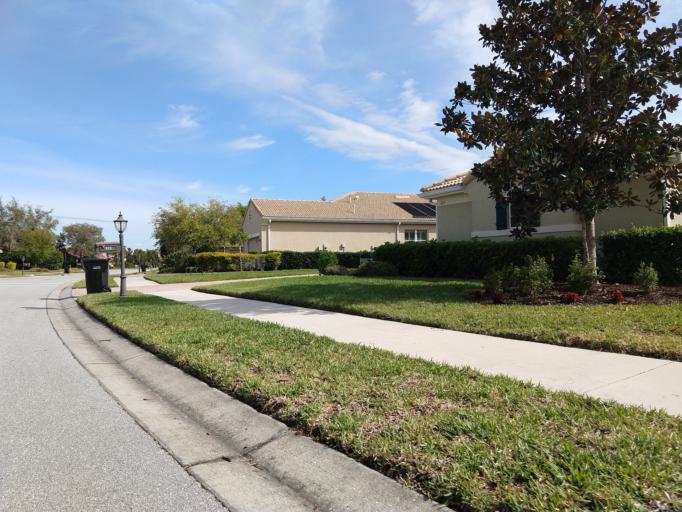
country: US
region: Florida
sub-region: Sarasota County
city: Nokomis
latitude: 27.1458
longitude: -82.3743
